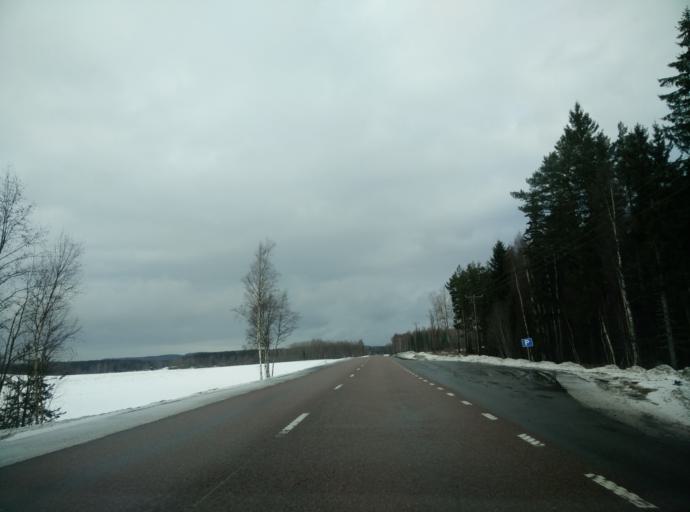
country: SE
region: Gaevleborg
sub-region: Hofors Kommun
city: Hofors
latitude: 60.5701
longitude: 16.4388
